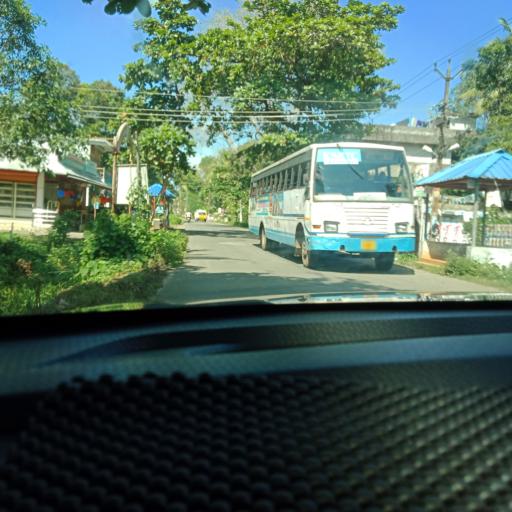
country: IN
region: Kerala
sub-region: Alappuzha
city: Mavelikara
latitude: 9.3059
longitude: 76.4568
